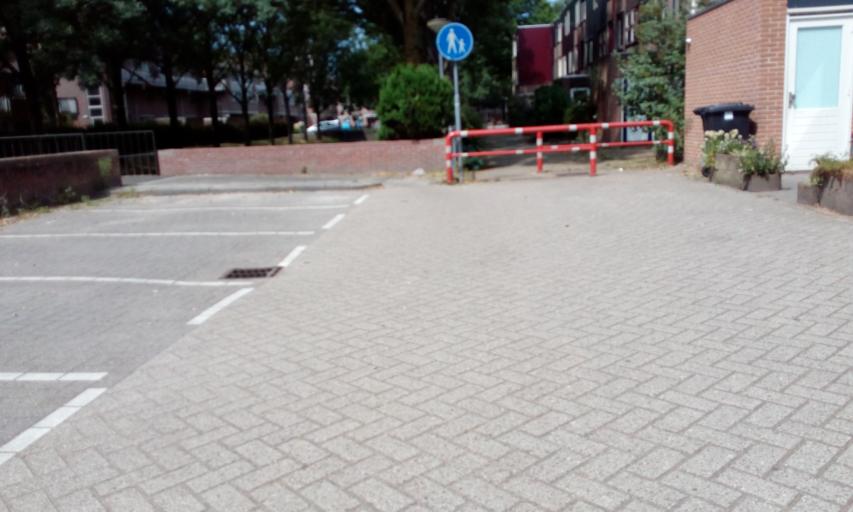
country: NL
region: South Holland
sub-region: Gemeente Capelle aan den IJssel
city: Capelle aan den IJssel
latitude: 51.9455
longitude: 4.5643
